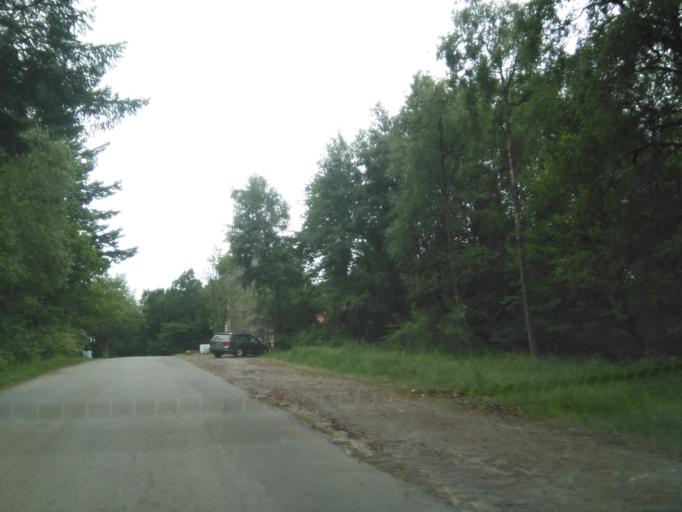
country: DK
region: Capital Region
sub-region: Bornholm Kommune
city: Akirkeby
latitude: 55.1122
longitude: 14.8901
